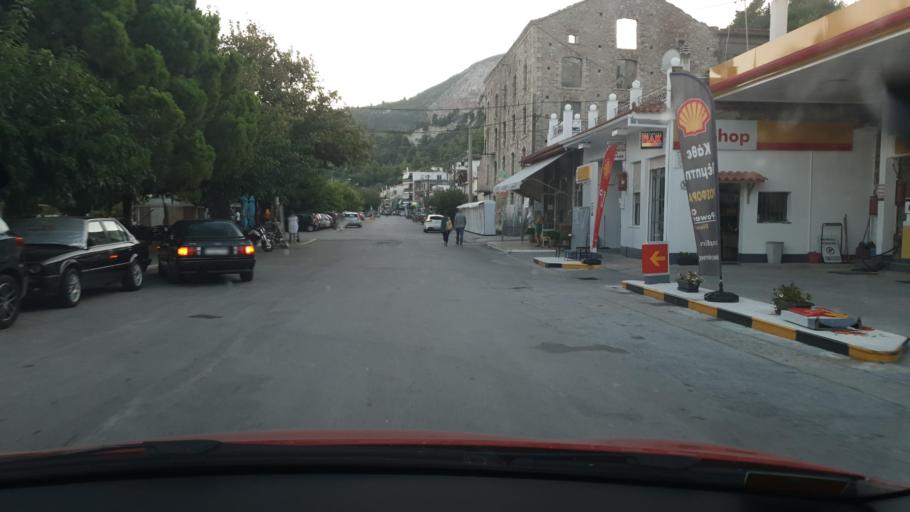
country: GR
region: Central Greece
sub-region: Nomos Evvoias
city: Kymi
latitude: 38.6315
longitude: 24.1245
